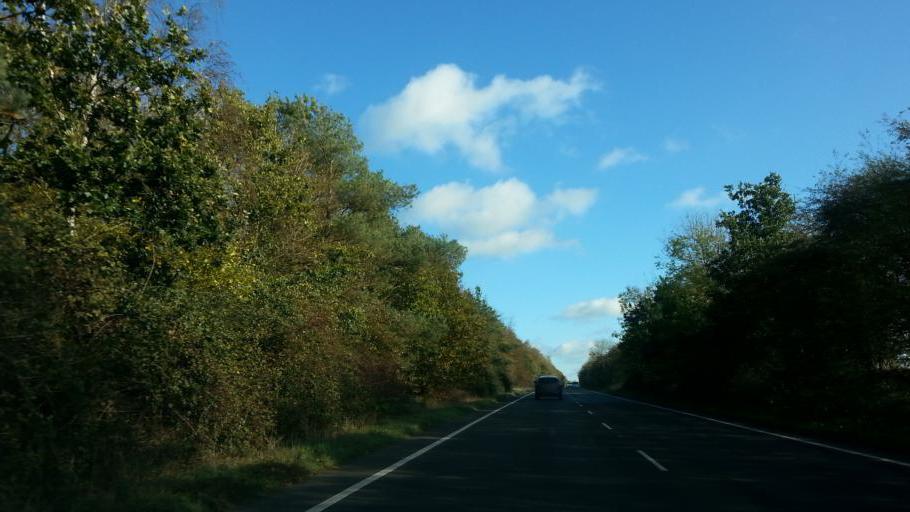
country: GB
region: England
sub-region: Norfolk
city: Loddon
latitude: 52.4857
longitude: 1.5005
